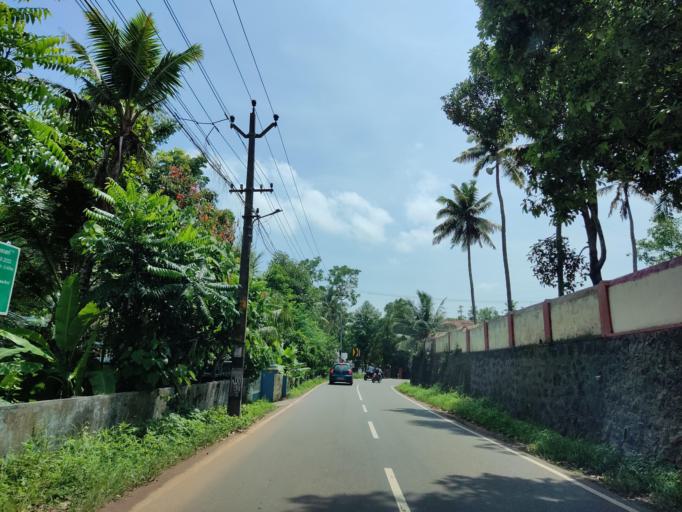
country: IN
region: Kerala
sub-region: Alappuzha
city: Chengannur
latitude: 9.3015
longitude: 76.5858
